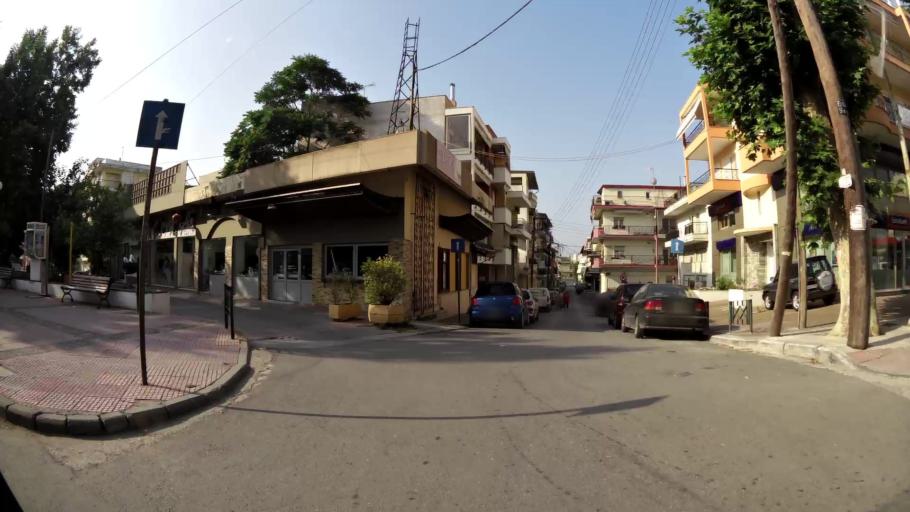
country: GR
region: Central Macedonia
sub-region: Nomos Thessalonikis
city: Evosmos
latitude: 40.6668
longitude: 22.9153
